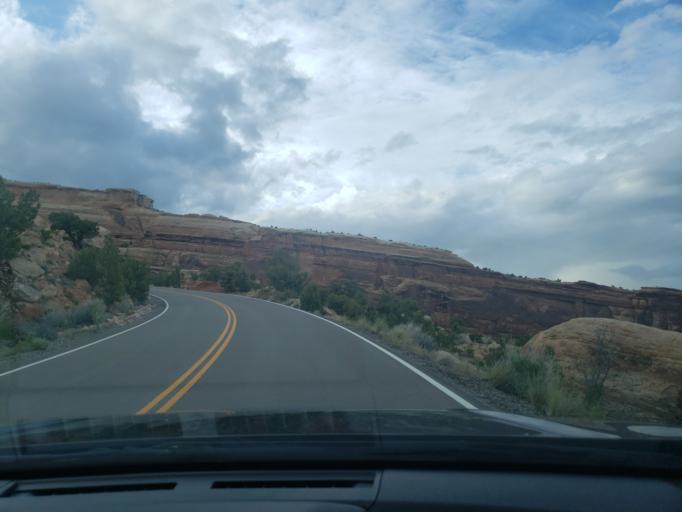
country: US
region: Colorado
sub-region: Mesa County
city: Redlands
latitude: 39.0275
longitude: -108.6413
